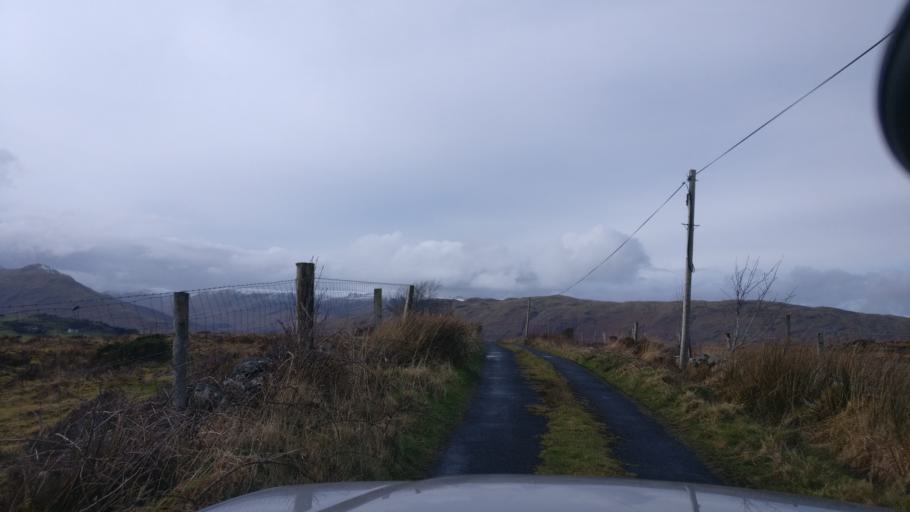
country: IE
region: Connaught
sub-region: County Galway
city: Oughterard
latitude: 53.5499
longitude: -9.4346
